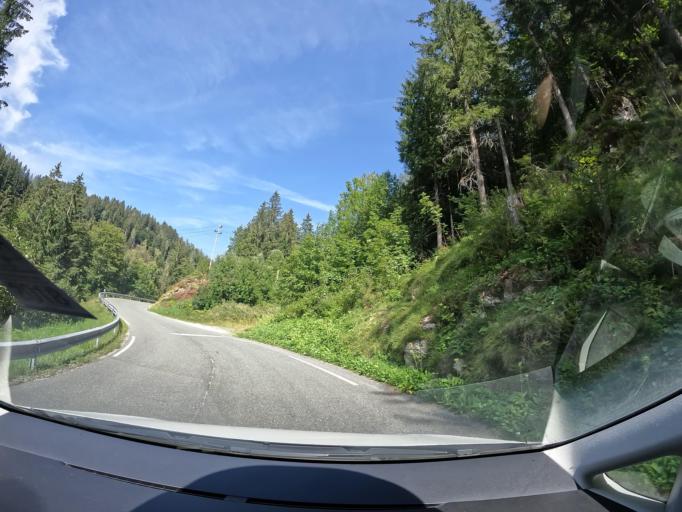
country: AT
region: Carinthia
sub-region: Politischer Bezirk Villach Land
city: Sankt Jakob
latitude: 46.5484
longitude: 14.0787
